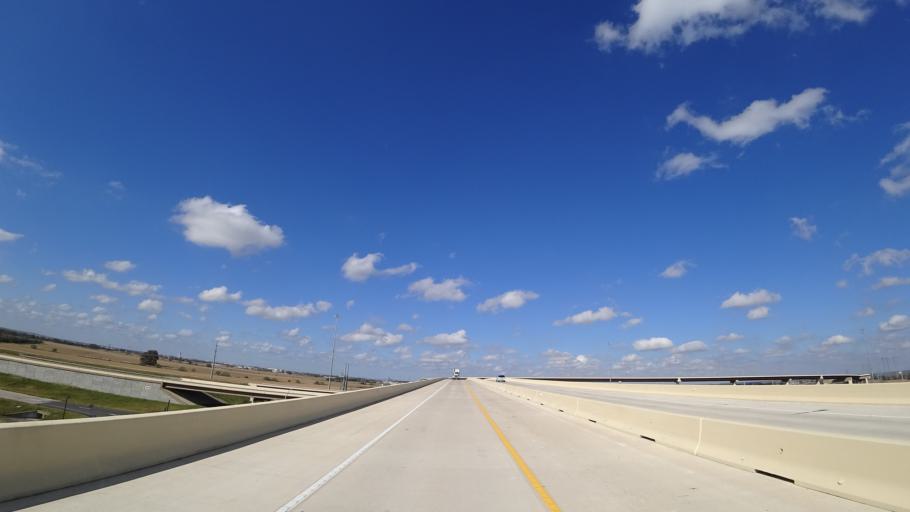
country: US
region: Texas
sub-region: Travis County
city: Garfield
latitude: 30.1930
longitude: -97.6230
